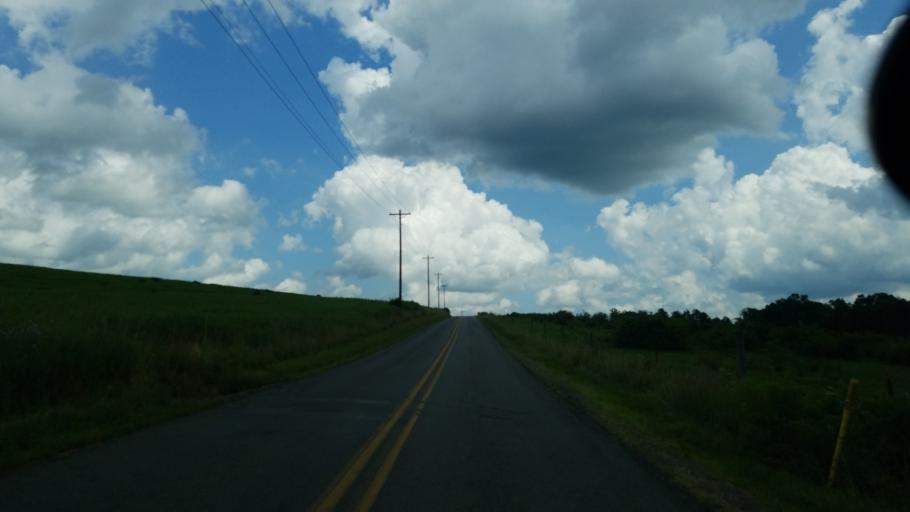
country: US
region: Pennsylvania
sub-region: Jefferson County
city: Brookville
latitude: 41.2329
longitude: -79.0777
